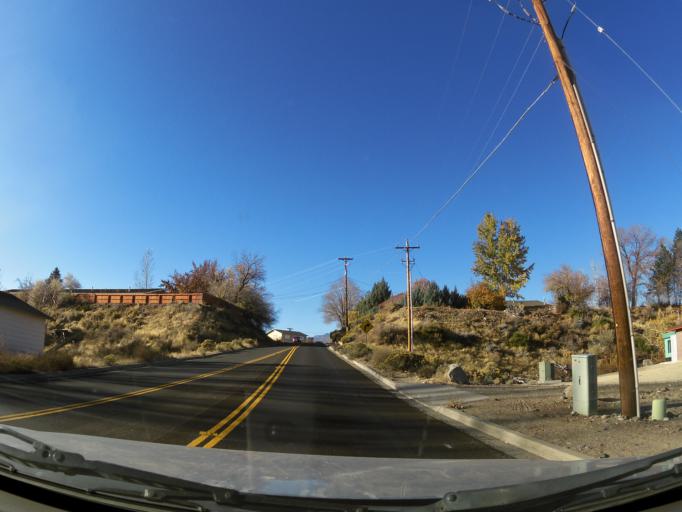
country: US
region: Nevada
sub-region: Douglas County
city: Gardnerville Ranchos
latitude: 38.9116
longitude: -119.7222
